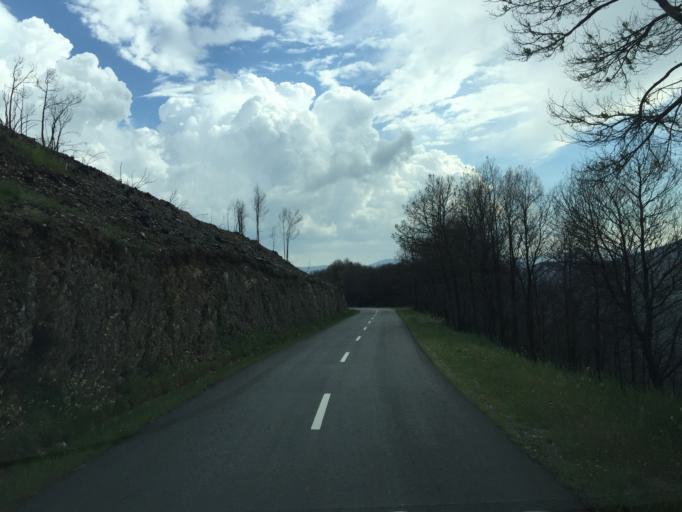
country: PT
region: Coimbra
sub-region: Arganil
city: Arganil
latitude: 40.1790
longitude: -7.9741
